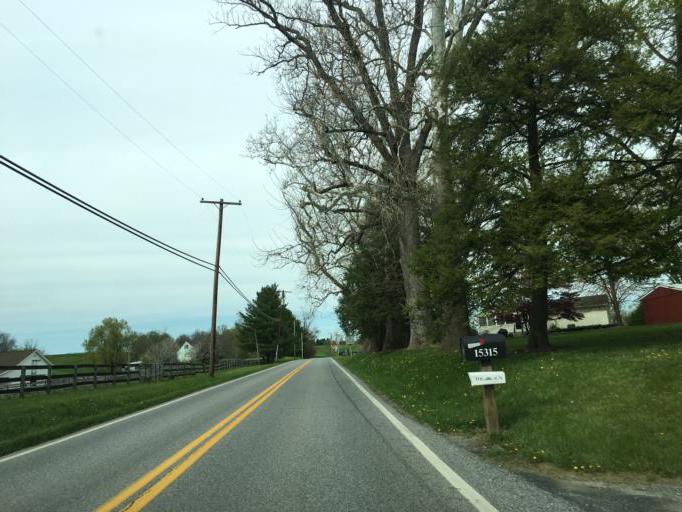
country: US
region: Maryland
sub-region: Baltimore County
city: Hunt Valley
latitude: 39.5460
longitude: -76.6110
